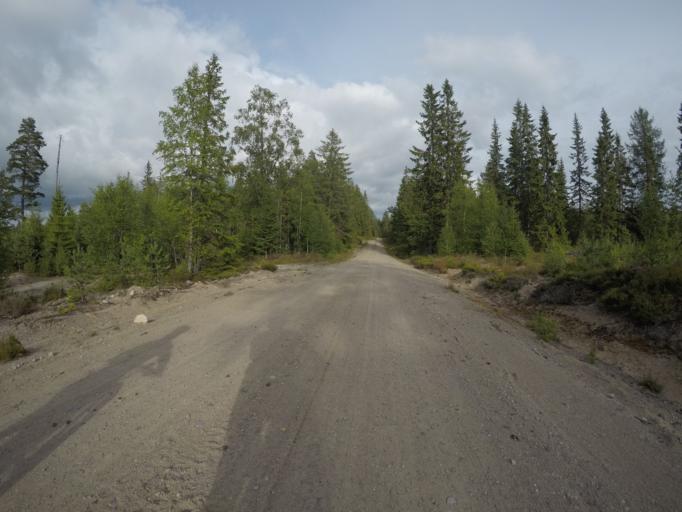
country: SE
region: Vaermland
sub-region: Filipstads Kommun
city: Lesjofors
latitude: 60.1982
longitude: 14.3186
